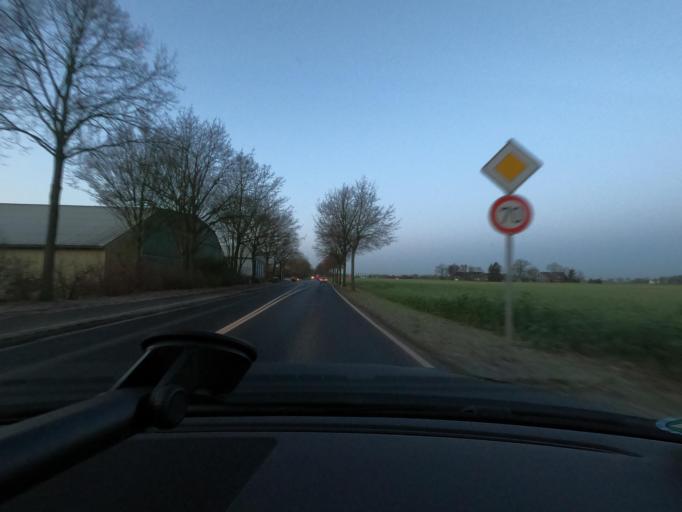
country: DE
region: North Rhine-Westphalia
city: Tonisvorst
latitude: 51.3290
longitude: 6.4842
